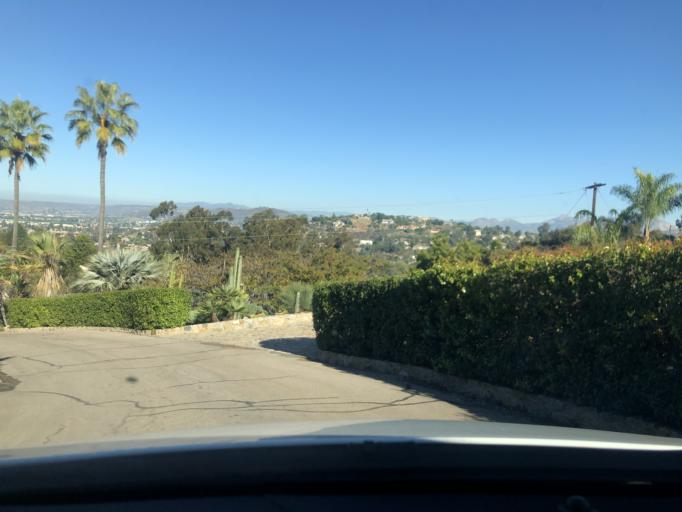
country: US
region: California
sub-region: San Diego County
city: Rancho San Diego
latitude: 32.7711
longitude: -116.9423
